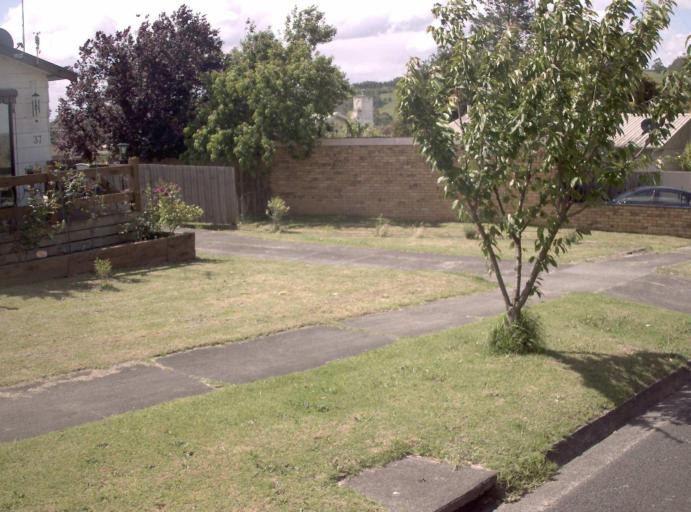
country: AU
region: Victoria
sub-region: Latrobe
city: Morwell
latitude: -38.1635
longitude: 146.3665
